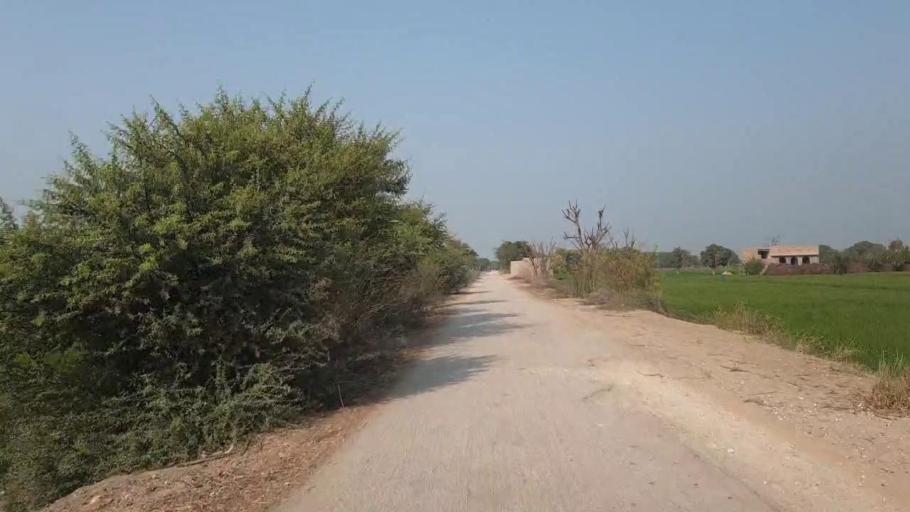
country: PK
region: Sindh
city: Hala
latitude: 25.8663
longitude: 68.4618
